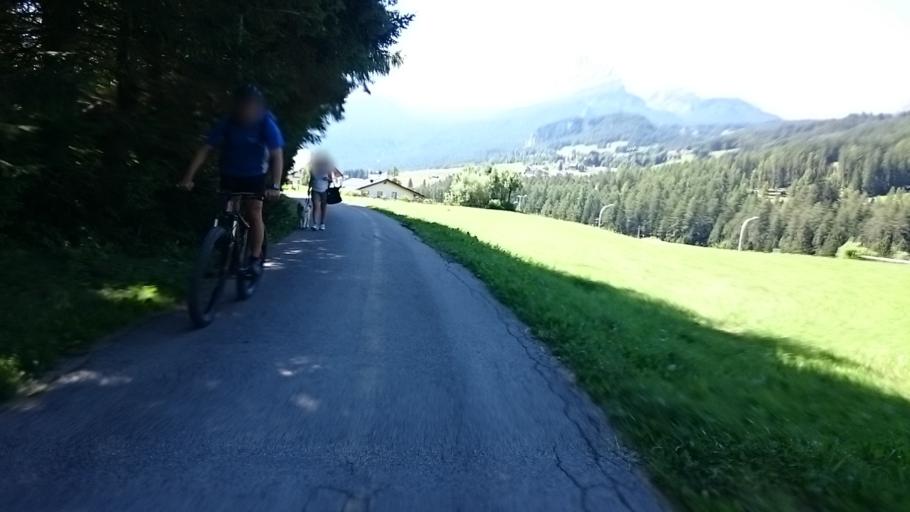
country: IT
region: Veneto
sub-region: Provincia di Belluno
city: Cortina d'Ampezzo
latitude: 46.5508
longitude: 12.1309
